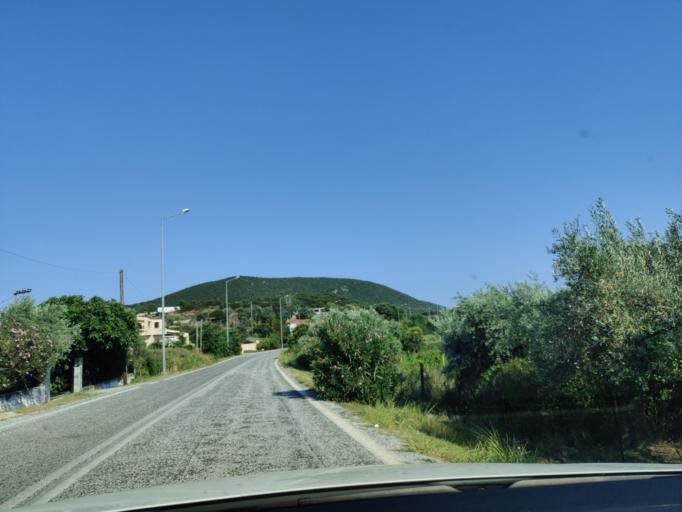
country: GR
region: East Macedonia and Thrace
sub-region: Nomos Kavalas
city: Nea Iraklitsa
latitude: 40.8558
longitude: 24.3118
